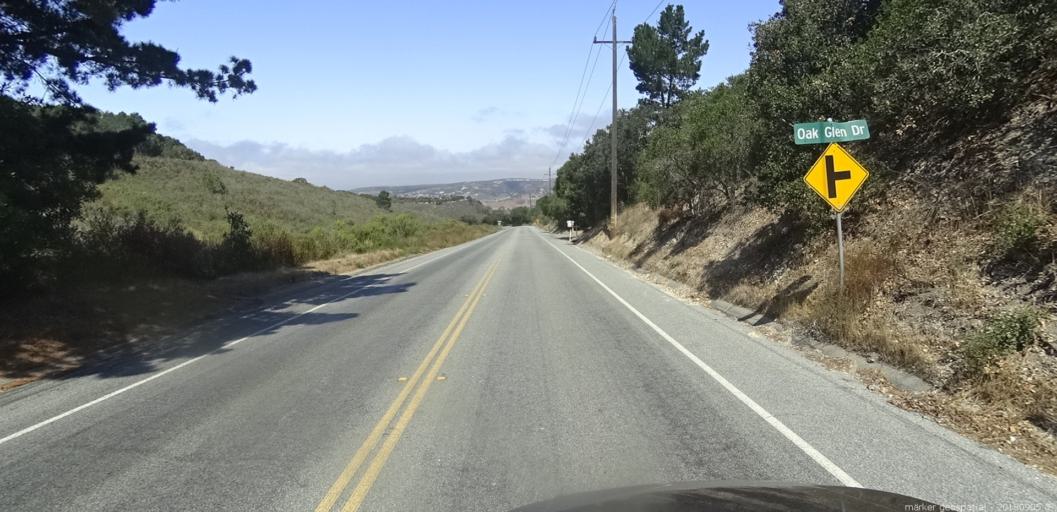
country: US
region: California
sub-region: Monterey County
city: Carmel Valley Village
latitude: 36.5499
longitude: -121.7533
